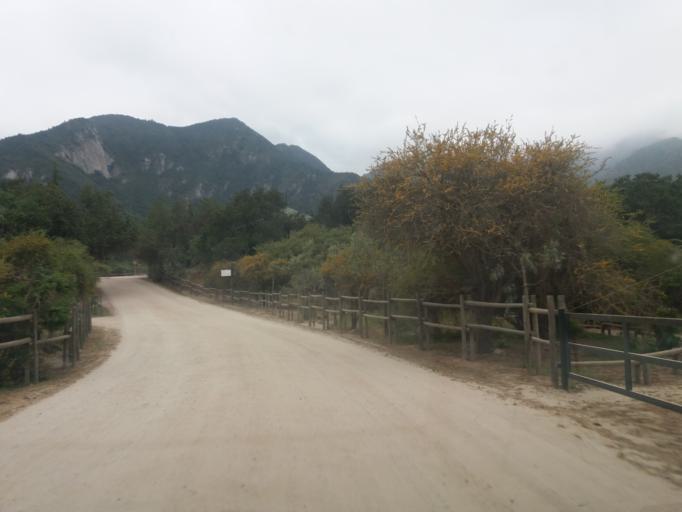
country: CL
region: Valparaiso
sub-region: Provincia de Marga Marga
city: Limache
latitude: -33.0276
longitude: -71.1399
